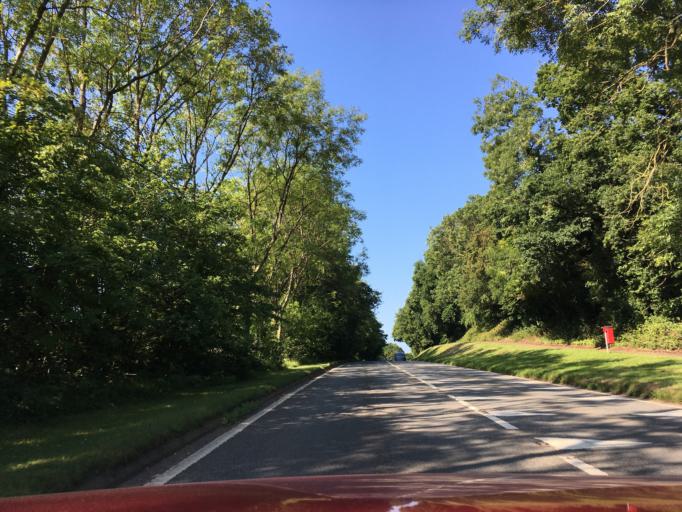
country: GB
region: England
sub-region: Gloucestershire
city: Lydney
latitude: 51.7114
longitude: -2.5581
